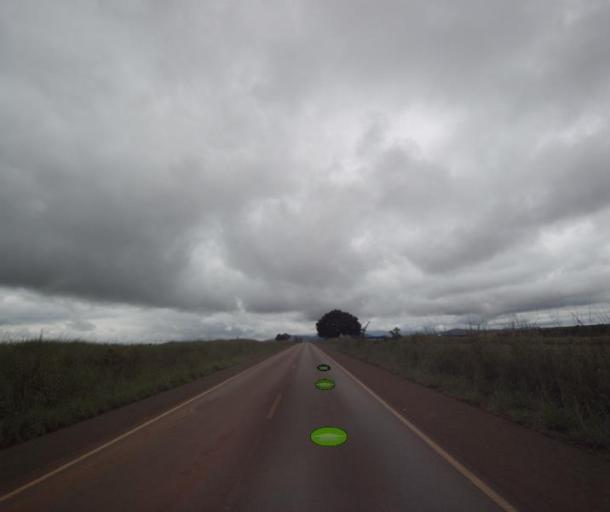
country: BR
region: Goias
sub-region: Barro Alto
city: Barro Alto
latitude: -14.8484
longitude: -49.0264
